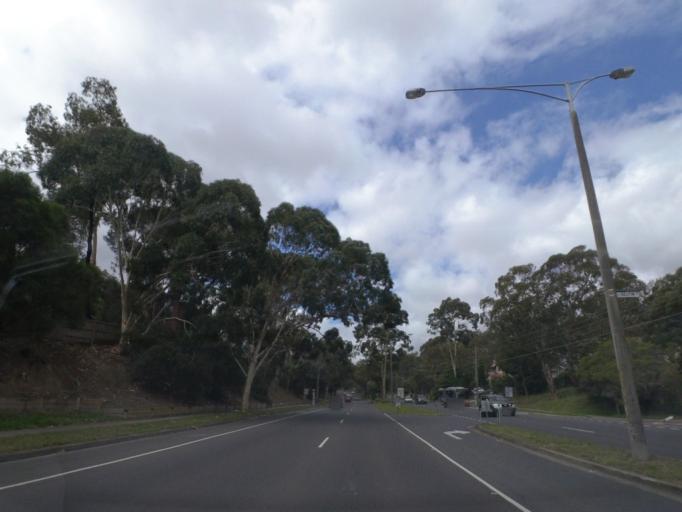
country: AU
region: Victoria
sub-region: Banyule
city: Greensborough
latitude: -37.6964
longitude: 145.1086
